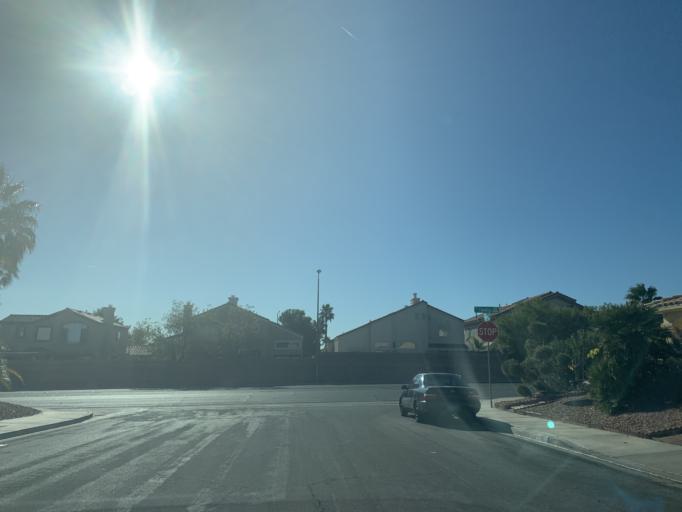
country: US
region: Nevada
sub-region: Clark County
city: Spring Valley
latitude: 36.1227
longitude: -115.2845
